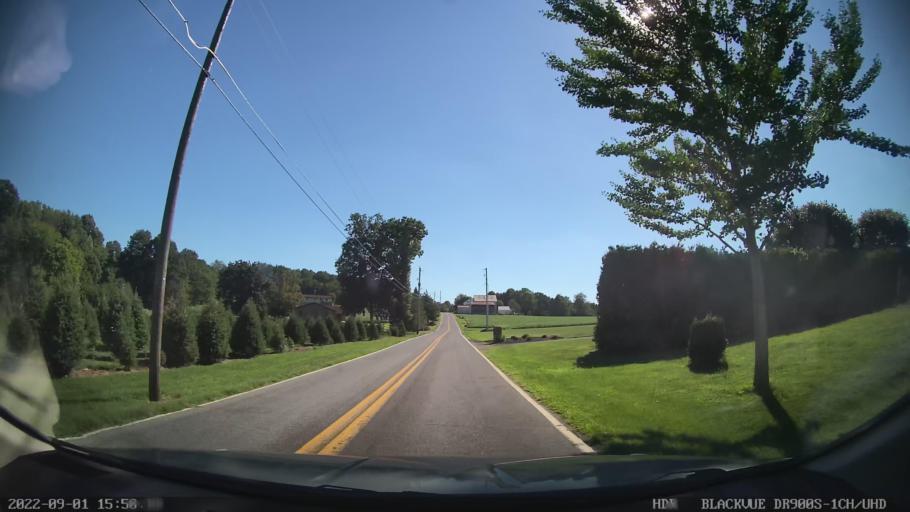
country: US
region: Pennsylvania
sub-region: Berks County
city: Topton
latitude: 40.4621
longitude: -75.7386
